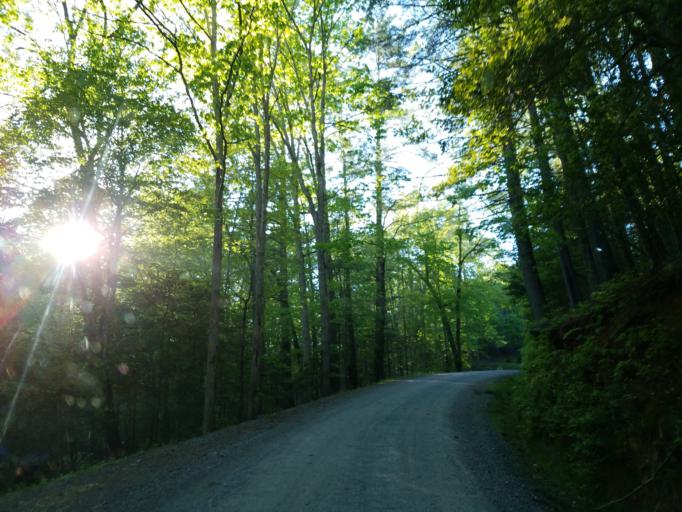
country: US
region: Georgia
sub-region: Fannin County
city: Blue Ridge
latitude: 34.7593
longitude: -84.2655
